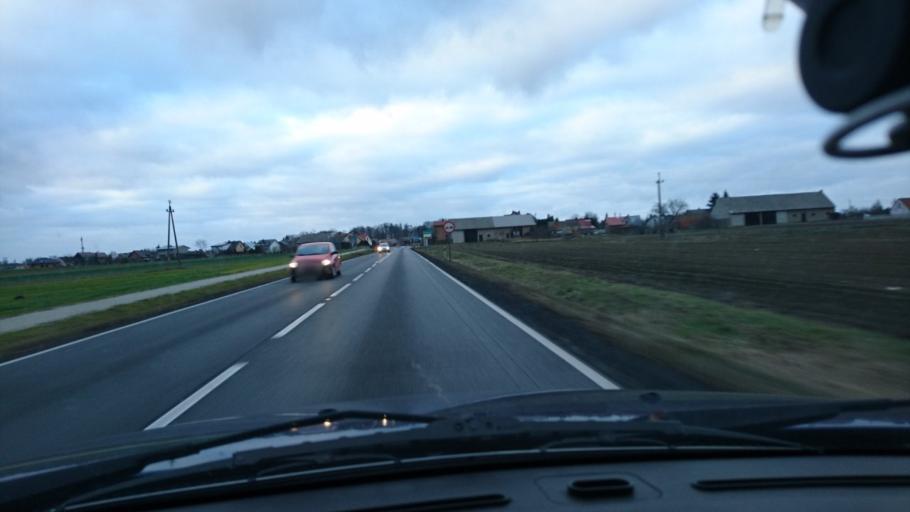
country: PL
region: Greater Poland Voivodeship
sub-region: Powiat kepinski
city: Opatow
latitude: 51.1743
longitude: 18.1450
